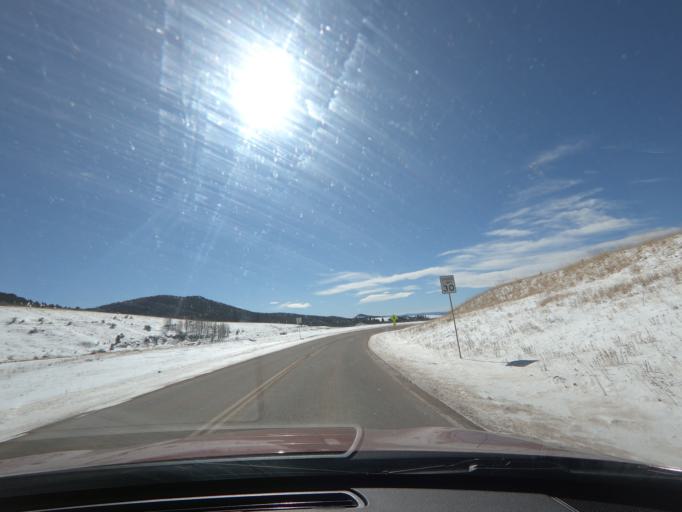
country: US
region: Colorado
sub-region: Teller County
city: Cripple Creek
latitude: 38.7121
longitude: -105.1323
